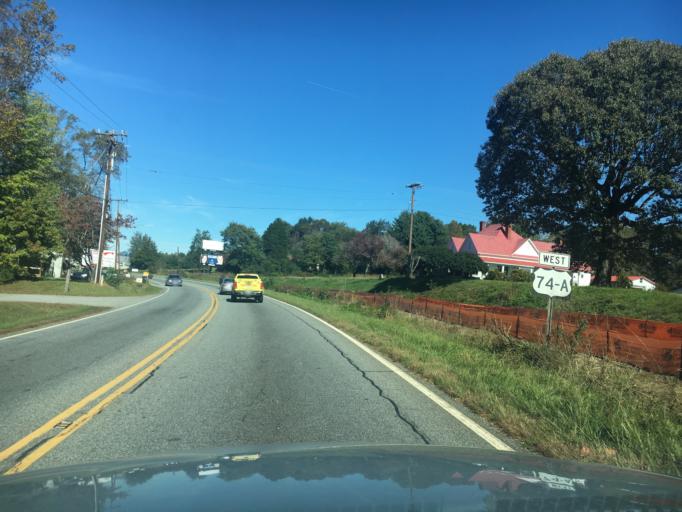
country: US
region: North Carolina
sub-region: Rutherford County
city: Rutherfordton
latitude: 35.3738
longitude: -81.9413
